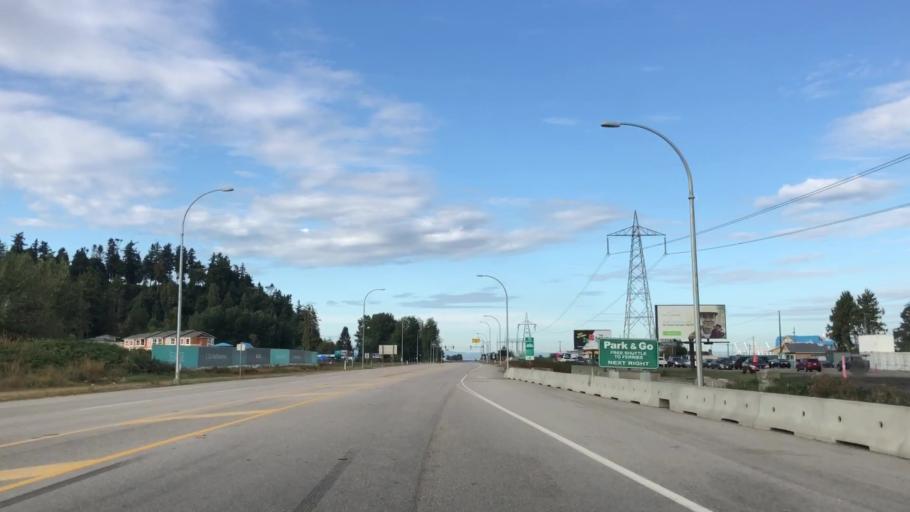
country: US
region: Washington
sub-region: Whatcom County
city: Point Roberts
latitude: 49.0312
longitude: -123.0930
